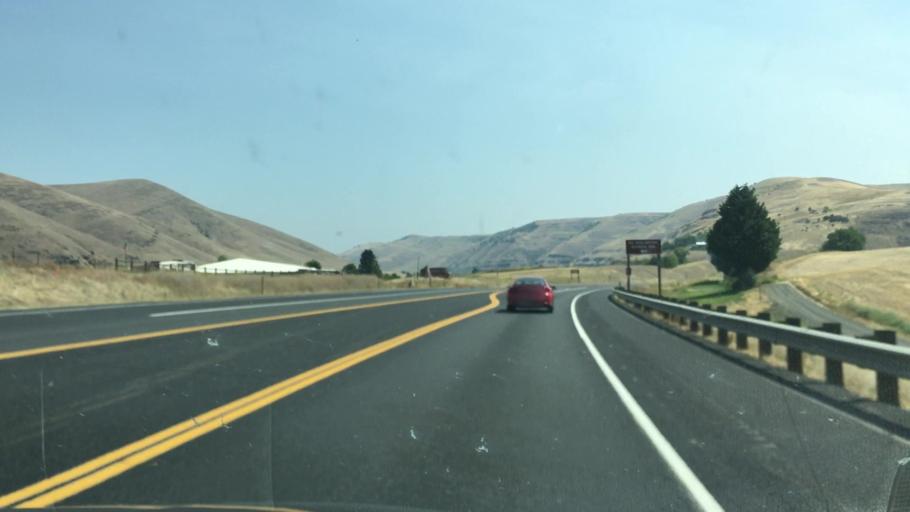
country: US
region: Idaho
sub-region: Nez Perce County
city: Lapwai
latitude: 46.4460
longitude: -116.8256
